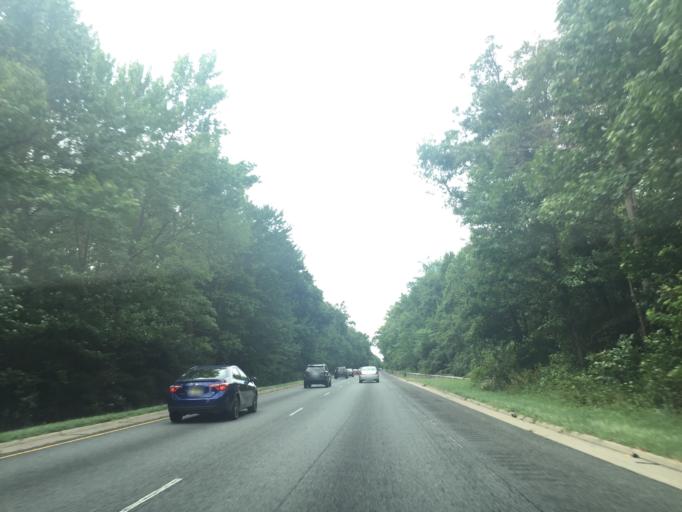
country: US
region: Maryland
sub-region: Anne Arundel County
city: Jessup
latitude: 39.1283
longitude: -76.7631
